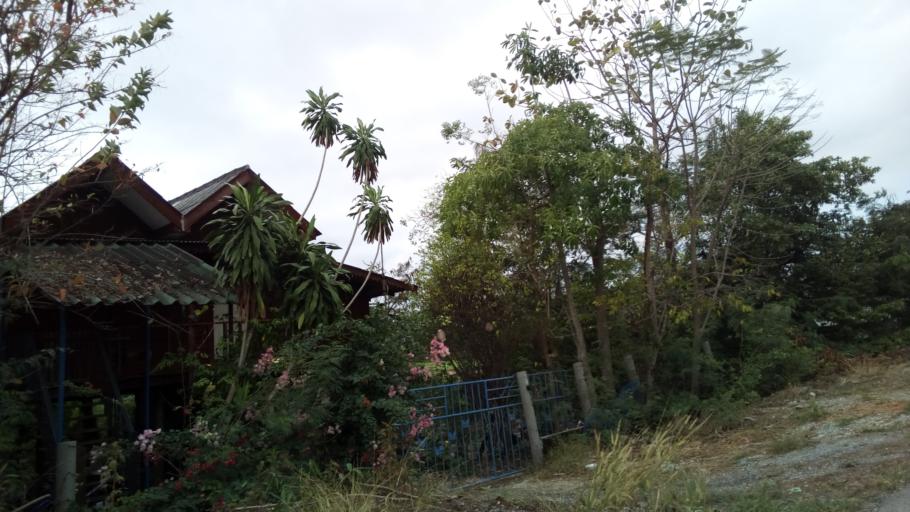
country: TH
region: Pathum Thani
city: Nong Suea
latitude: 14.0734
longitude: 100.8944
